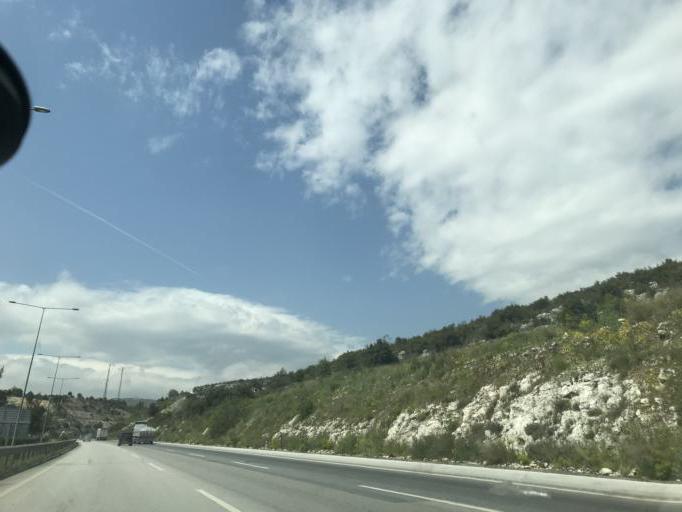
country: TR
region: Mersin
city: Tarsus
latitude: 37.1483
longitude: 34.8412
